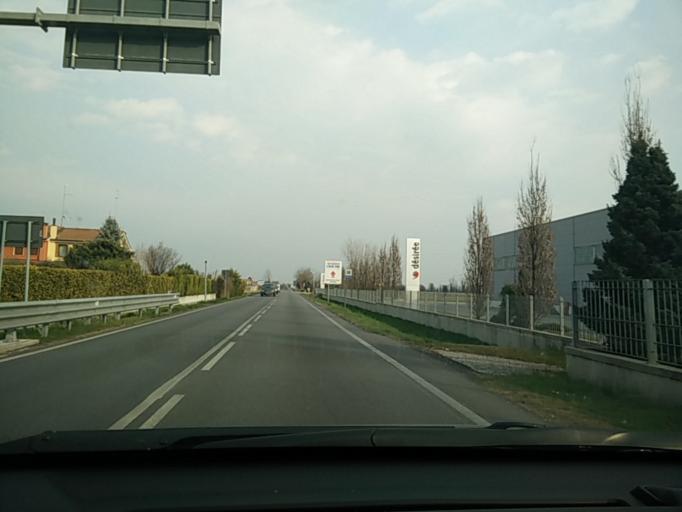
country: IT
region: Veneto
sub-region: Provincia di Treviso
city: San Michele di Piave
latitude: 45.8118
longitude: 12.3501
